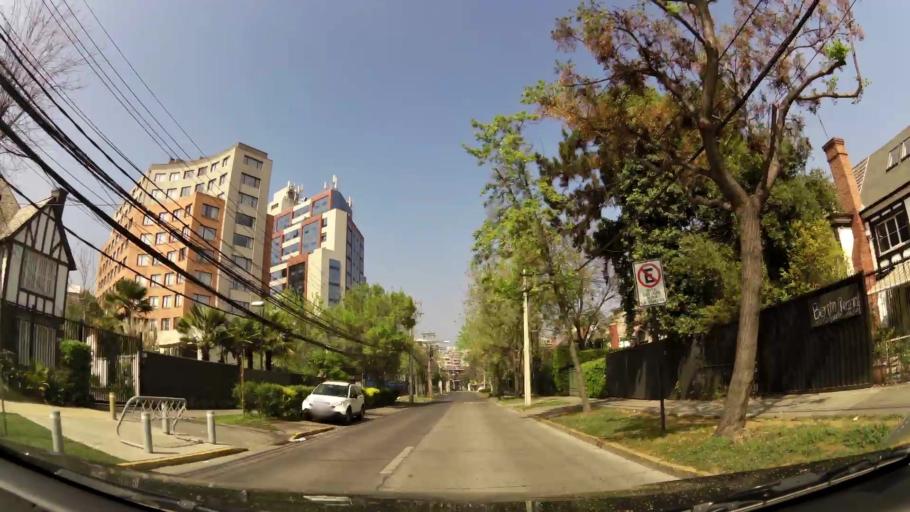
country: CL
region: Santiago Metropolitan
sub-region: Provincia de Santiago
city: Villa Presidente Frei, Nunoa, Santiago, Chile
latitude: -33.4025
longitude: -70.5961
